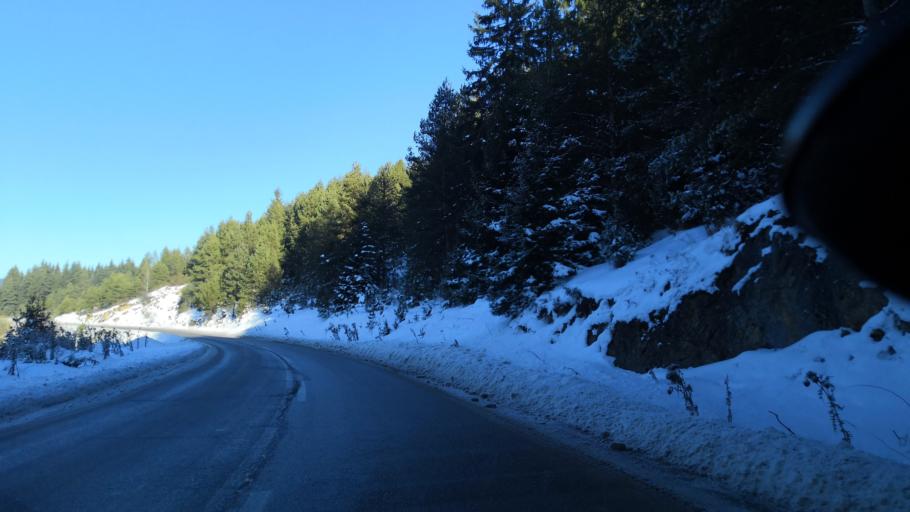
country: BA
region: Republika Srpska
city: Sokolac
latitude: 43.9877
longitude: 18.8702
